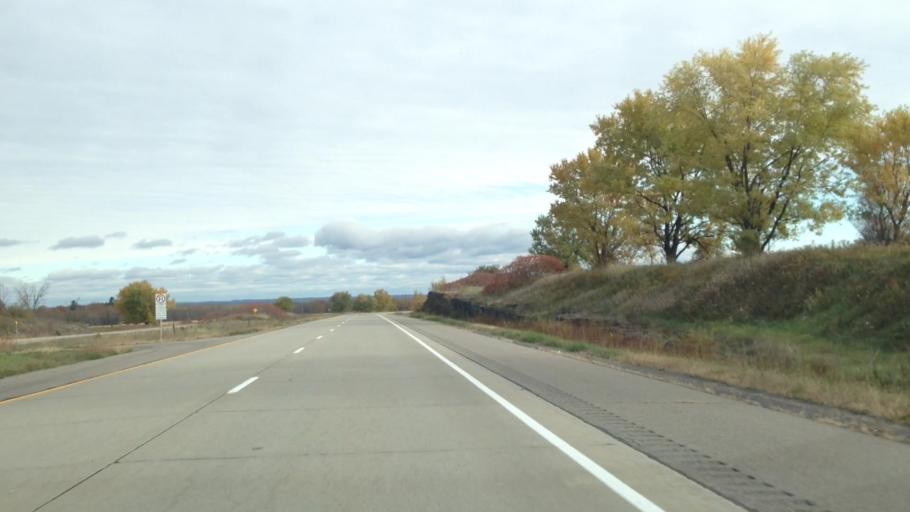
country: CA
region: Ontario
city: Hawkesbury
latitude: 45.5602
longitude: -74.5125
